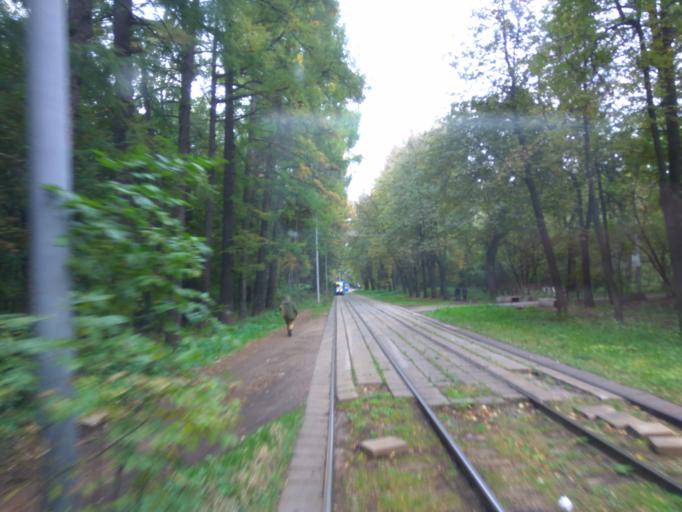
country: RU
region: Moscow
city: Metrogorodok
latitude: 55.7866
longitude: 37.7586
